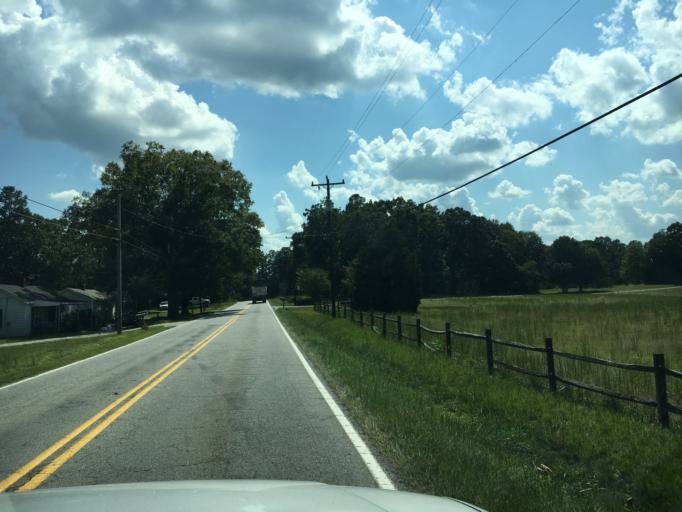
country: US
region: South Carolina
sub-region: Spartanburg County
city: Woodruff
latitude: 34.7249
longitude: -82.0455
